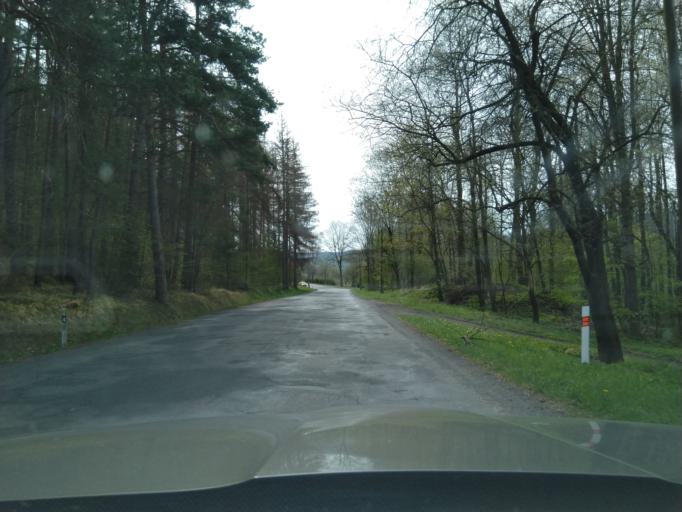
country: CZ
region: Plzensky
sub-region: Okres Klatovy
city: Kasperske Hory
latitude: 49.1890
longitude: 13.6249
